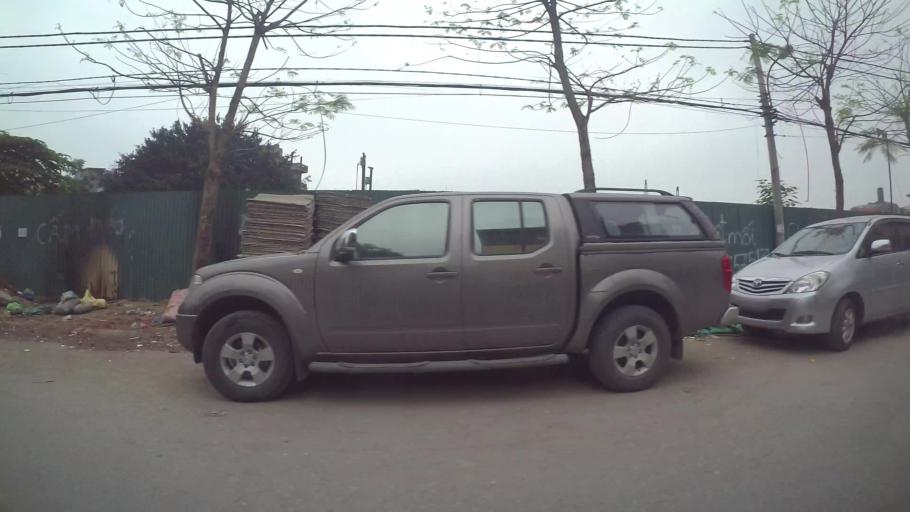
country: VN
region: Ha Noi
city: Hai BaTrung
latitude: 20.9896
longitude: 105.8597
